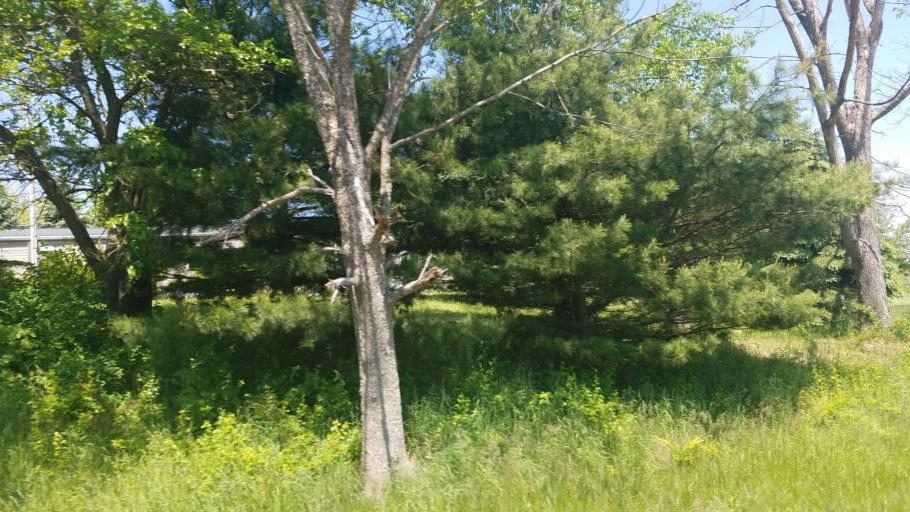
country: US
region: Ohio
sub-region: Muskingum County
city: Frazeysburg
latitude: 40.2093
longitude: -82.2481
